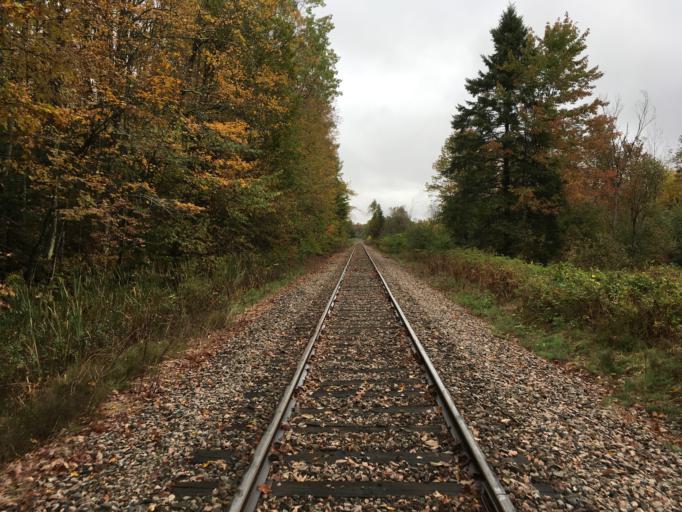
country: US
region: Vermont
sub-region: Orleans County
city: Newport
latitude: 44.8587
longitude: -72.2064
